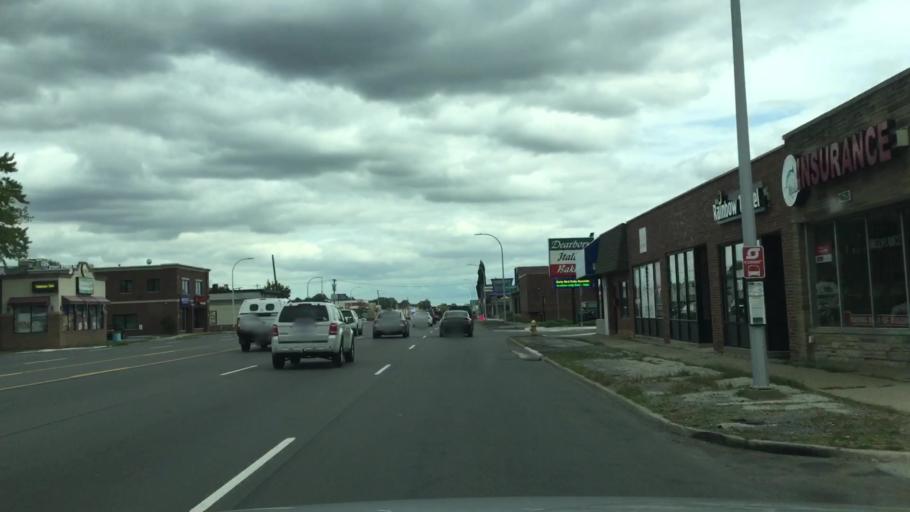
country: US
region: Michigan
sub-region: Wayne County
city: Dearborn Heights
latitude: 42.3268
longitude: -83.2791
